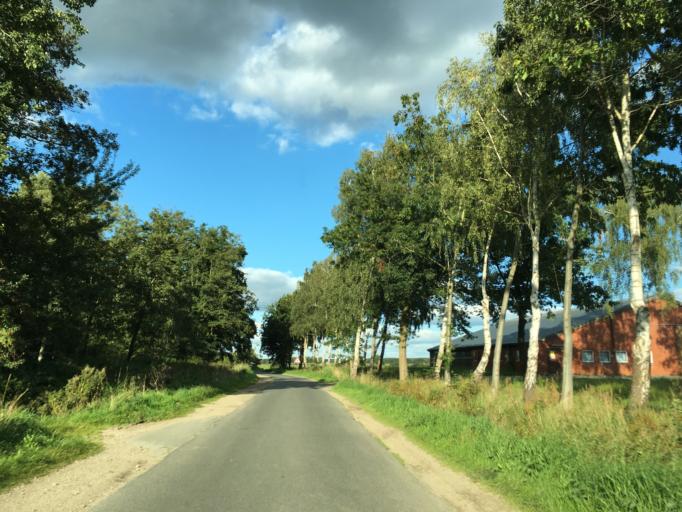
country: DE
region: Lower Saxony
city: Salzhausen
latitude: 53.2330
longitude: 10.1745
